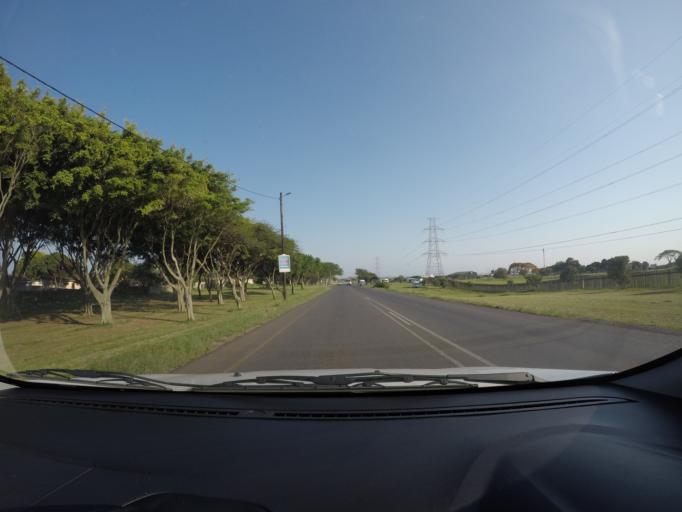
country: ZA
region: KwaZulu-Natal
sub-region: uThungulu District Municipality
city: Richards Bay
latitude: -28.7286
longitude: 32.0371
